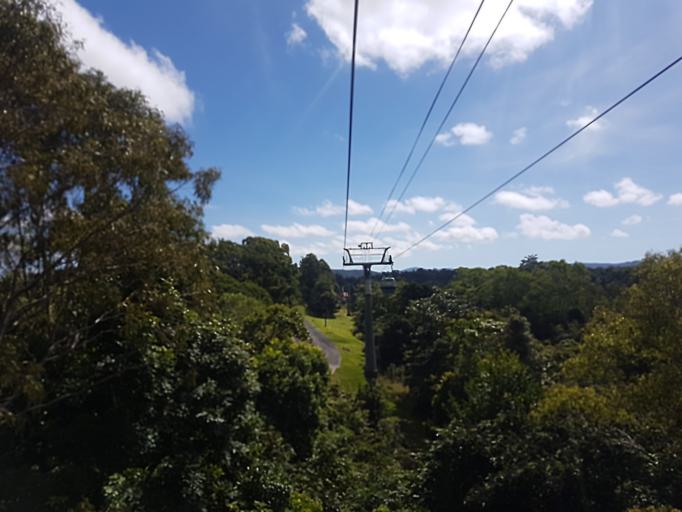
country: AU
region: Queensland
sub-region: Tablelands
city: Kuranda
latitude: -16.8234
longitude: 145.6410
